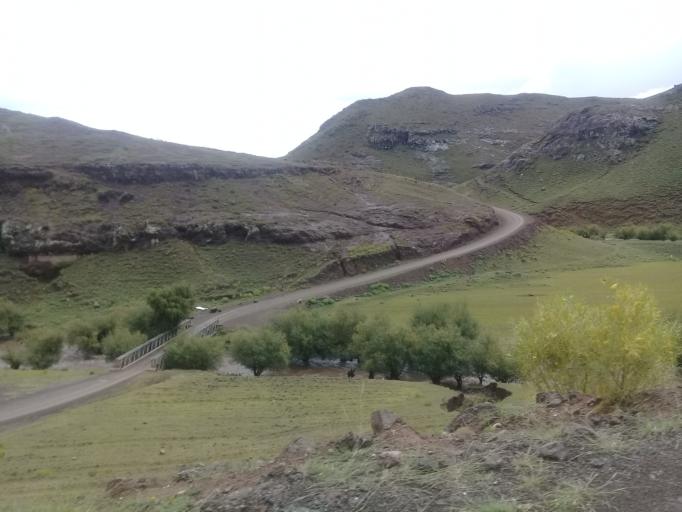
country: LS
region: Mokhotlong
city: Mokhotlong
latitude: -29.3341
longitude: 29.0272
